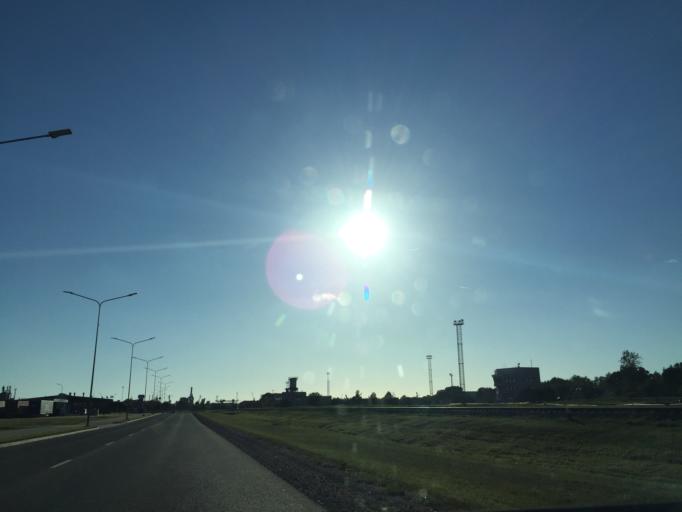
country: LV
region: Ventspils
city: Ventspils
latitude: 57.3946
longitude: 21.6193
